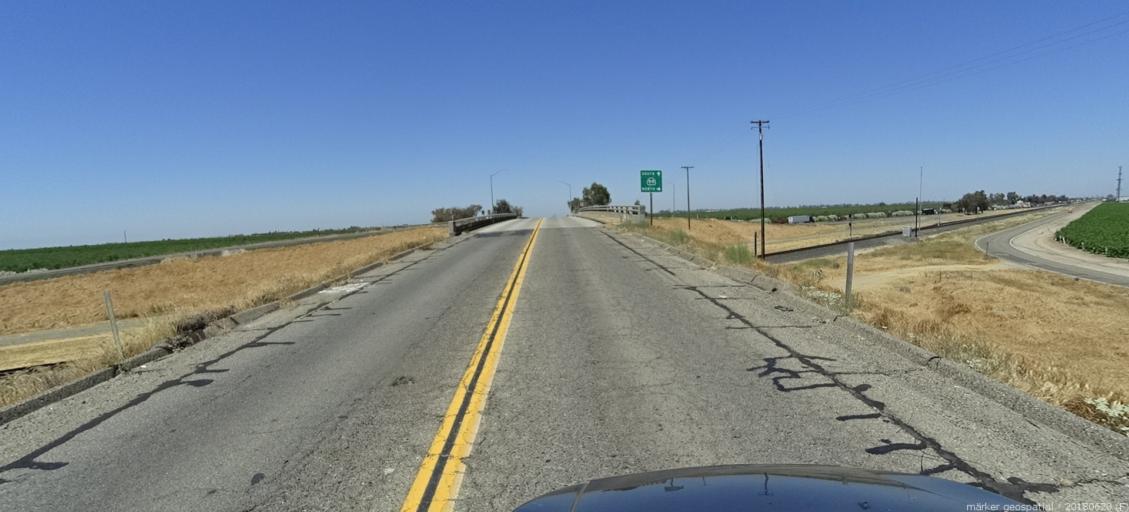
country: US
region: California
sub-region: Madera County
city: Parksdale
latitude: 36.8803
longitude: -119.9745
